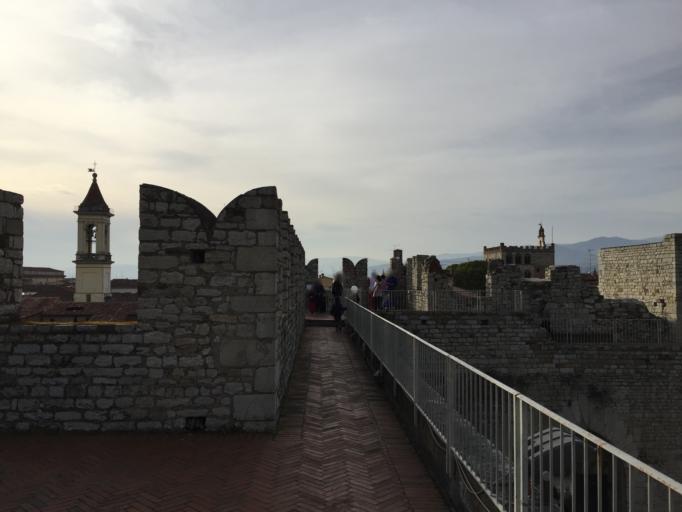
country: IT
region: Tuscany
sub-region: Provincia di Prato
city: Prato
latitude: 43.8788
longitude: 11.0985
